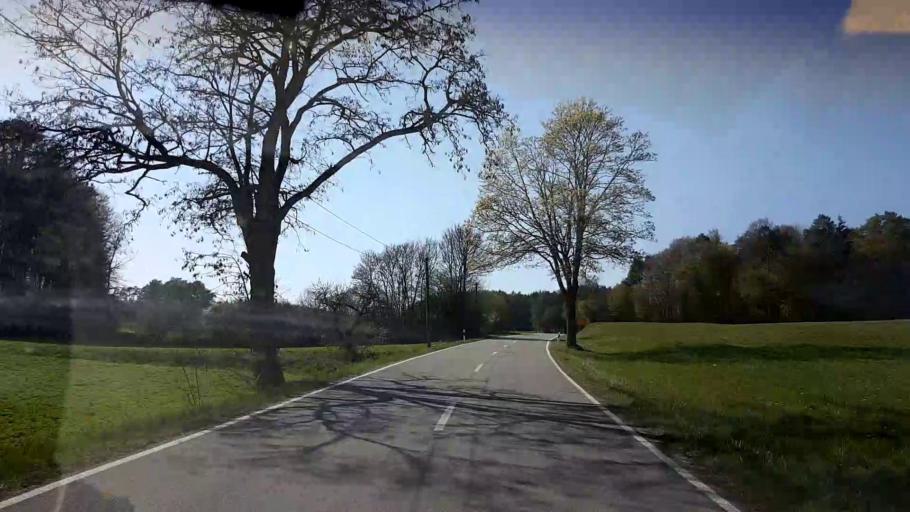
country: DE
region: Bavaria
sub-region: Upper Franconia
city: Pottenstein
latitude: 49.7912
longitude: 11.4163
